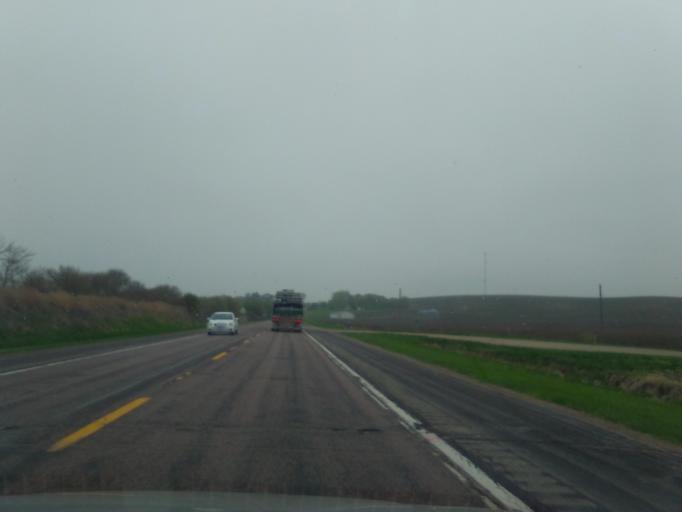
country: US
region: Nebraska
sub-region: Burt County
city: Oakland
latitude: 41.8142
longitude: -96.4739
